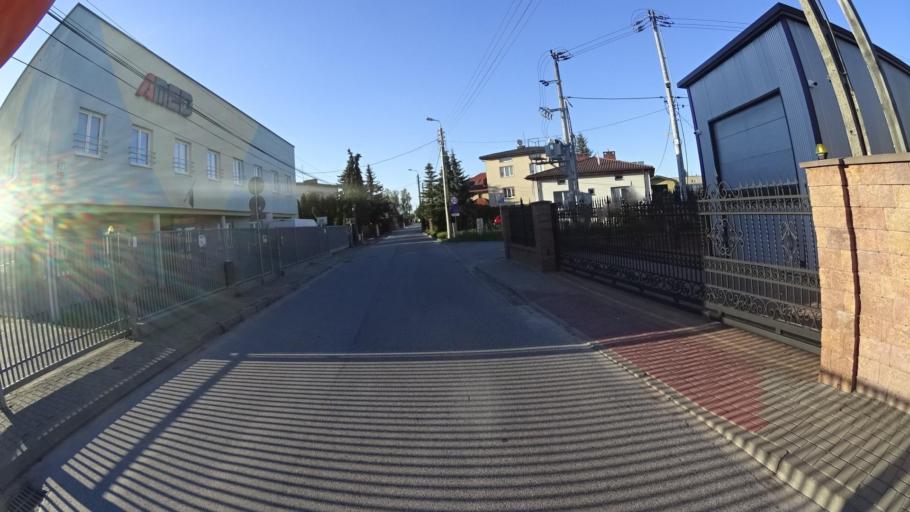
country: PL
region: Masovian Voivodeship
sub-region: Powiat pruszkowski
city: Raszyn
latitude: 52.1621
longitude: 20.9206
